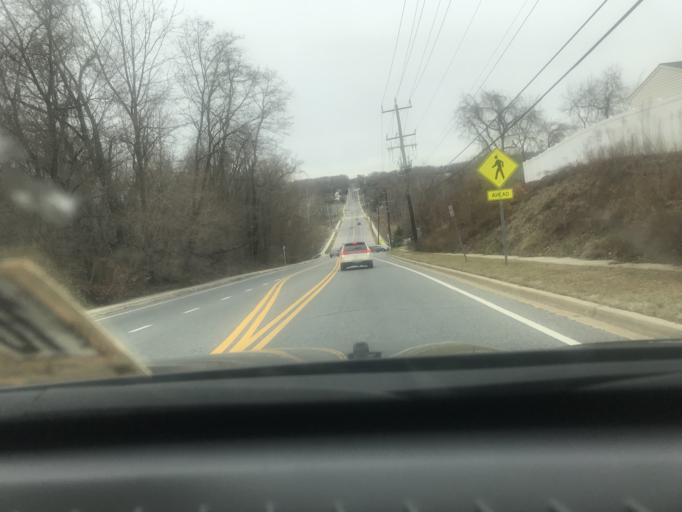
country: US
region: Maryland
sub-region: Prince George's County
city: Oxon Hill
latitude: 38.7870
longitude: -76.9683
